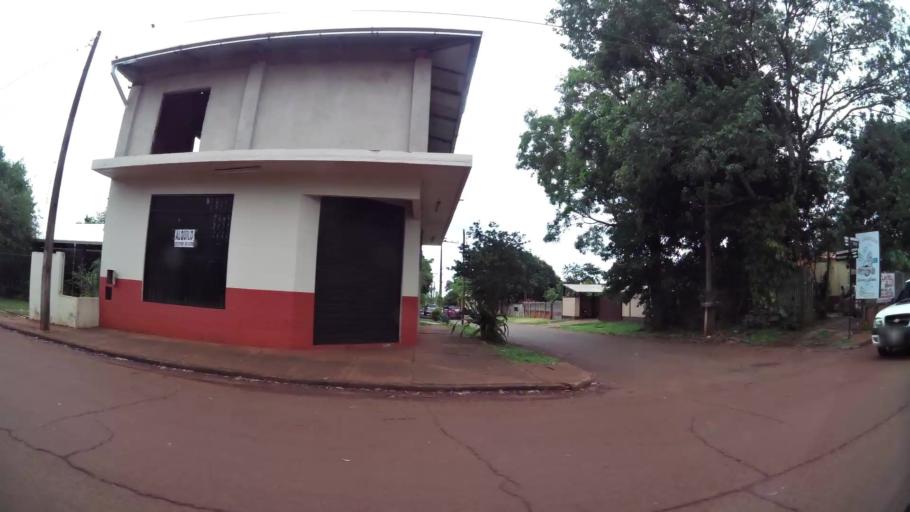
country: PY
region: Alto Parana
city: Ciudad del Este
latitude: -25.4022
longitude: -54.6261
